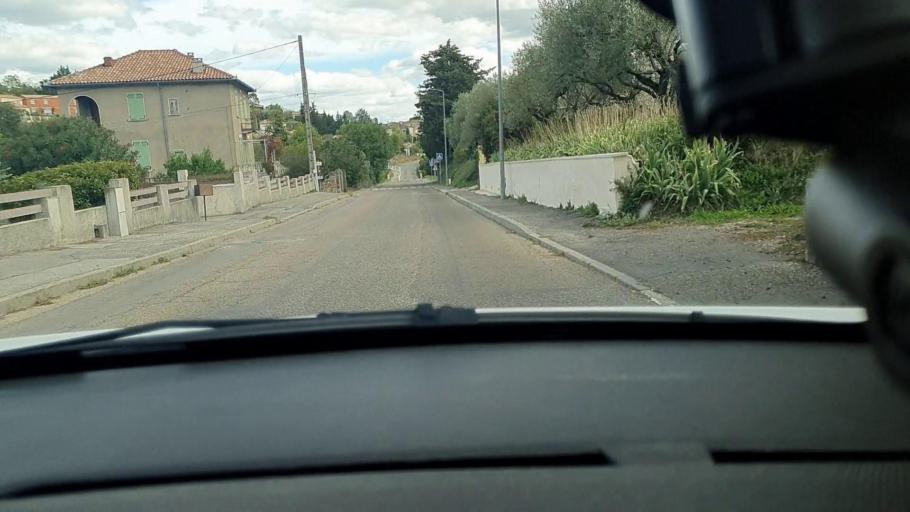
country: FR
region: Languedoc-Roussillon
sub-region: Departement du Gard
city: Les Mages
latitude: 44.2270
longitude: 4.1692
